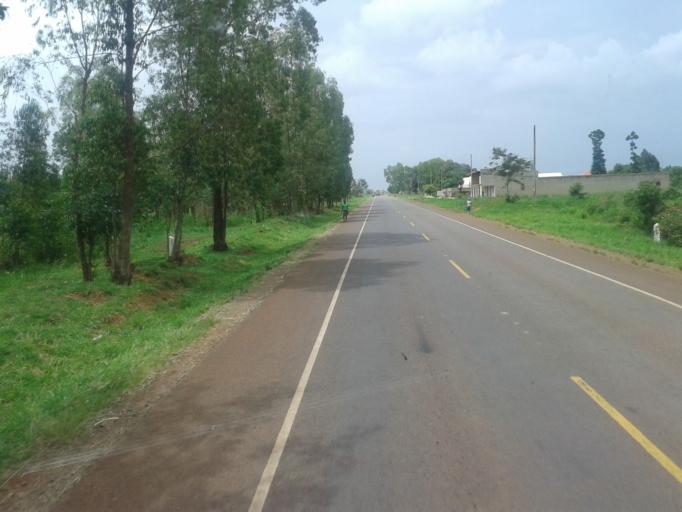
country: UG
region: Western Region
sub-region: Kiryandongo District
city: Kiryandongo
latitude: 1.9652
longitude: 32.1512
